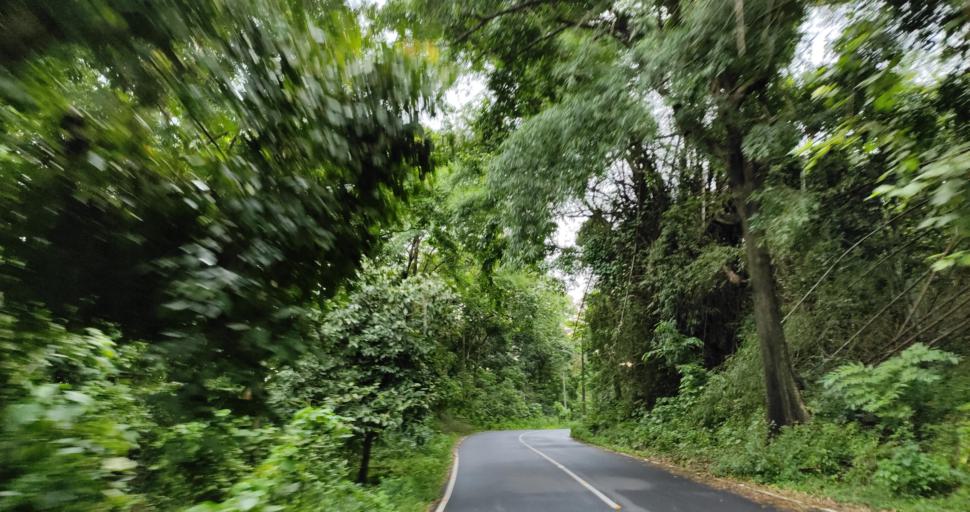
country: IN
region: Kerala
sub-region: Ernakulam
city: Angamali
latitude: 10.2982
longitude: 76.4564
